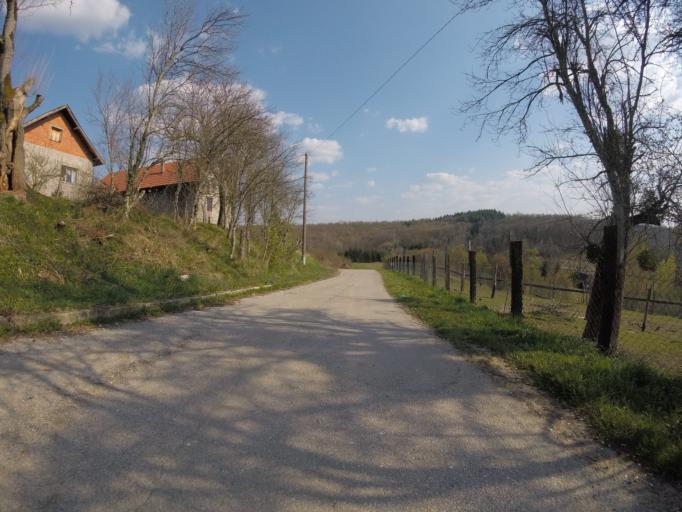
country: HR
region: Zagrebacka
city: Mraclin
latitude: 45.5051
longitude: 16.0059
